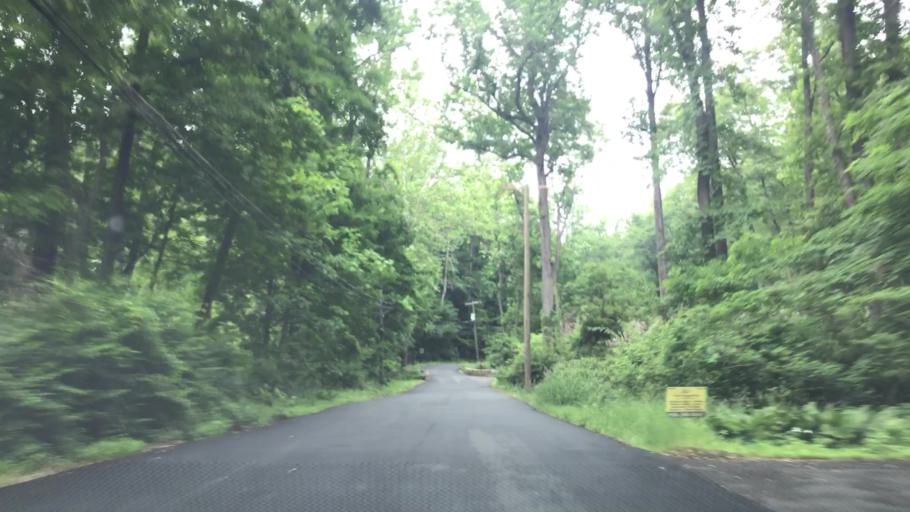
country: US
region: New Jersey
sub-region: Hunterdon County
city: Lebanon
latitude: 40.6656
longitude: -74.8335
